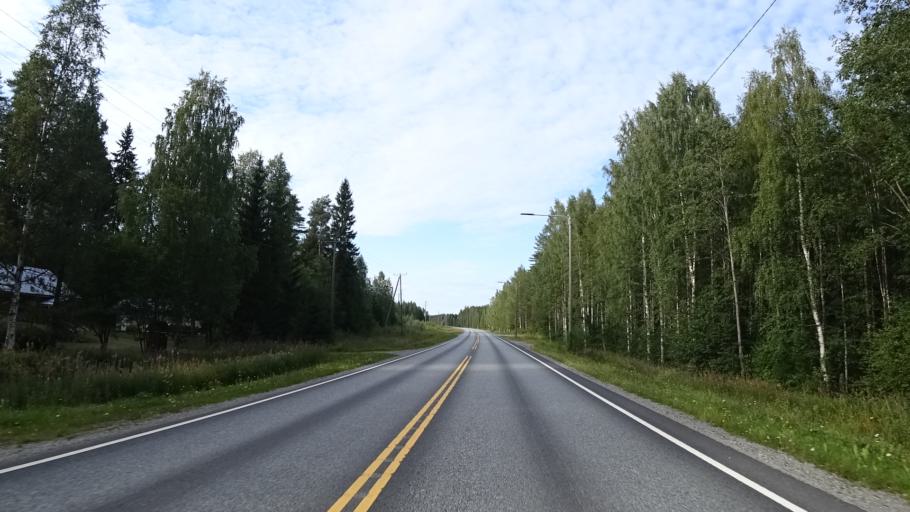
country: FI
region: North Karelia
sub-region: Joensuu
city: Eno
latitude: 62.8663
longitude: 30.2006
